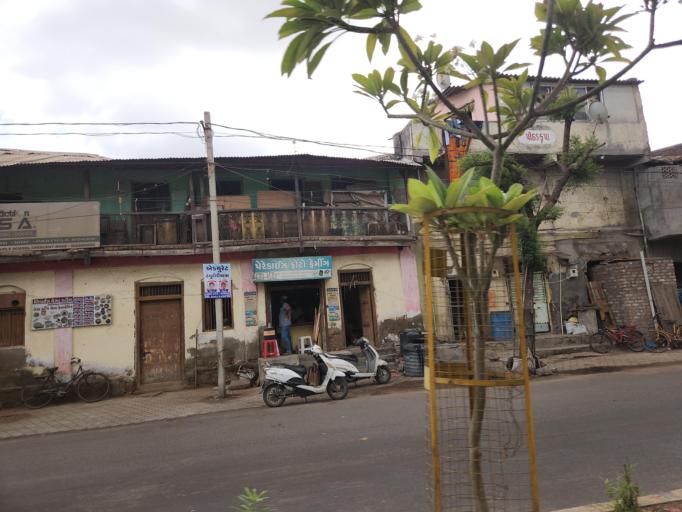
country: IN
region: Gujarat
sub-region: Bhavnagar
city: Bhavnagar
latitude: 21.7752
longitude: 72.1504
